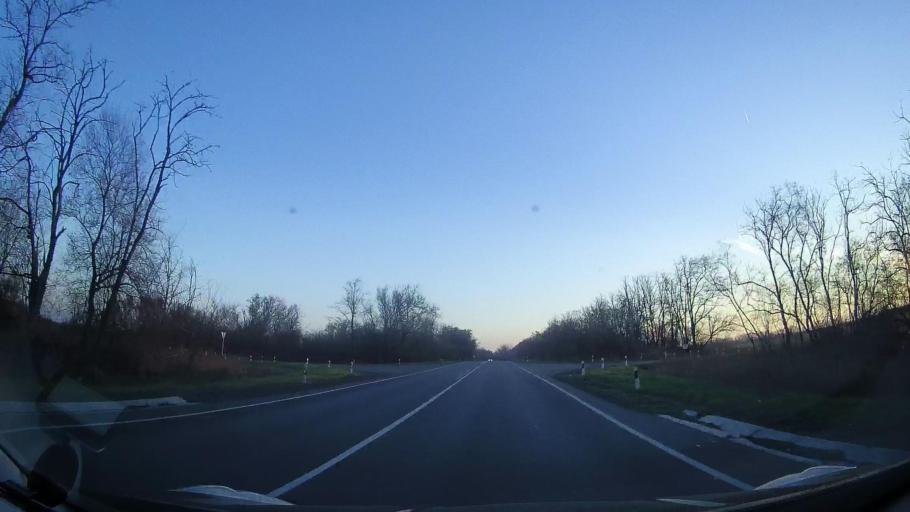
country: RU
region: Rostov
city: Bagayevskaya
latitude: 47.1052
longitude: 40.2767
